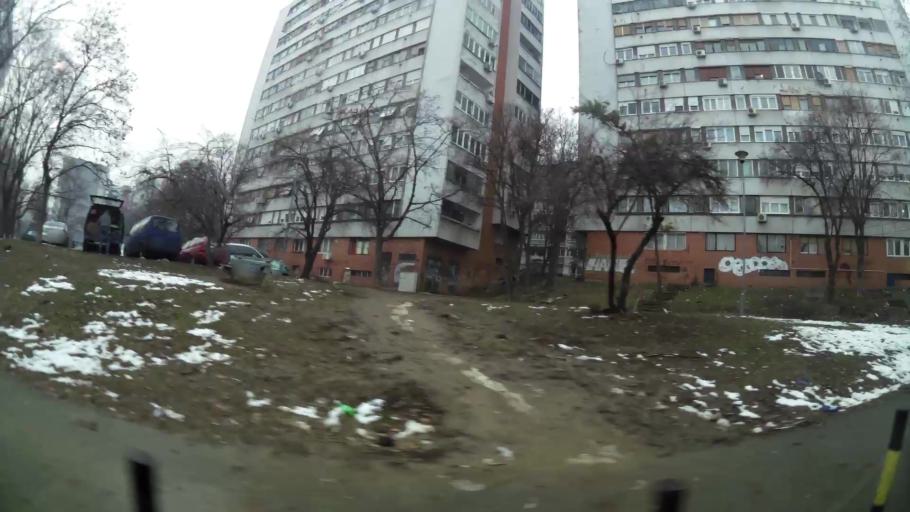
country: RS
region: Central Serbia
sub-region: Belgrade
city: Zvezdara
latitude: 44.7799
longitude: 20.5102
